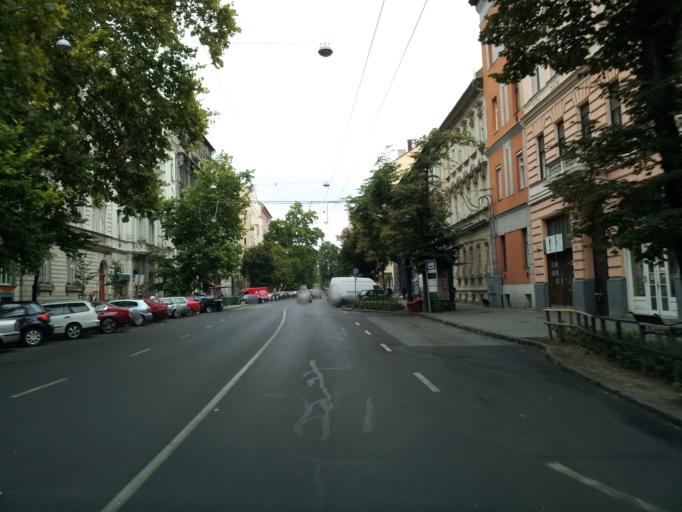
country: HU
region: Budapest
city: Budapest VII. keruelet
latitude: 47.5074
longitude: 19.0777
